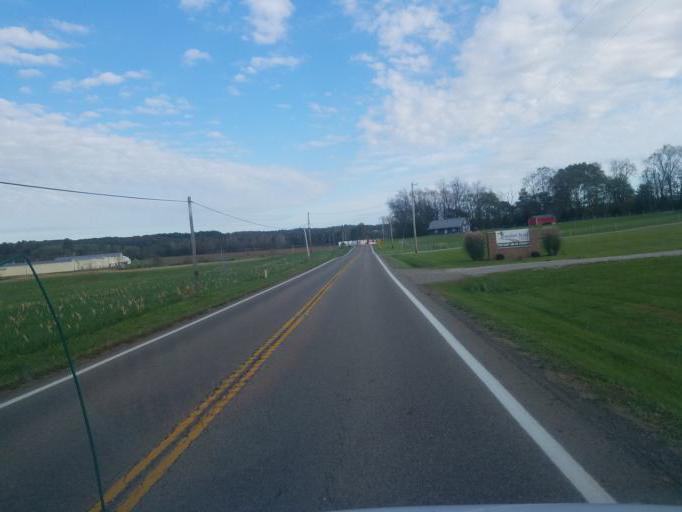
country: US
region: Ohio
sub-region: Holmes County
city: Millersburg
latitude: 40.6377
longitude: -81.9284
